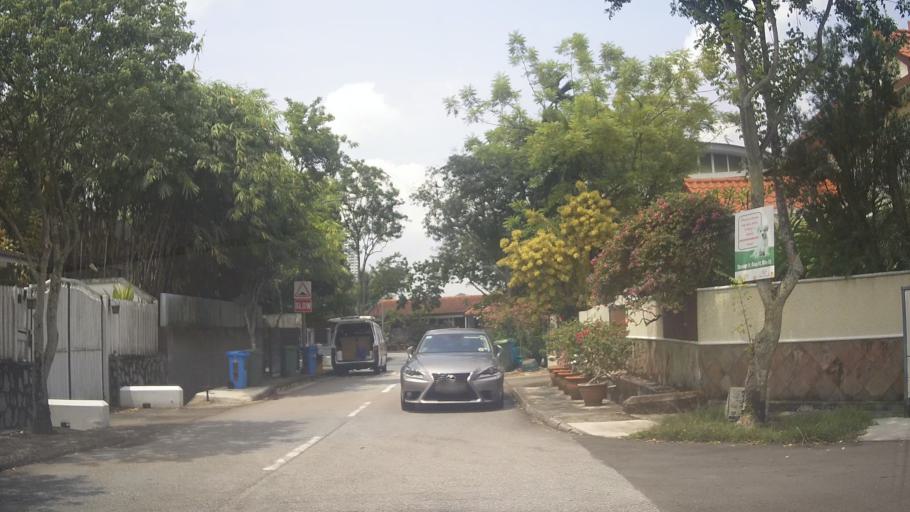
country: SG
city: Singapore
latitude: 1.3158
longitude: 103.7877
